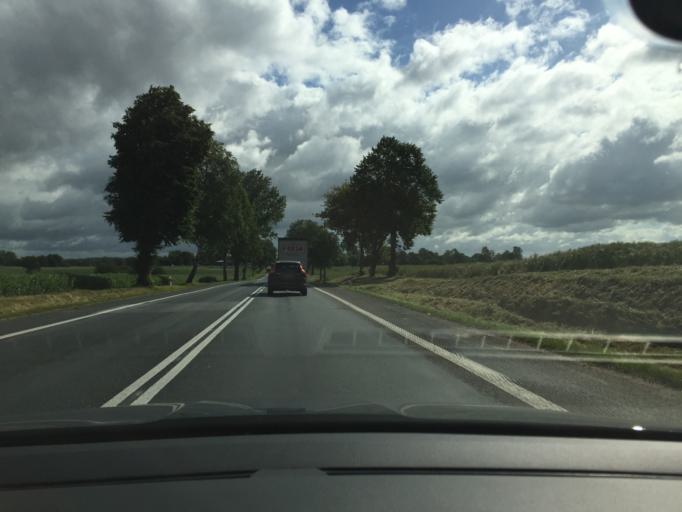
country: PL
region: West Pomeranian Voivodeship
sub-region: Powiat kolobrzeski
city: Goscino
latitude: 53.9893
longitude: 15.7286
